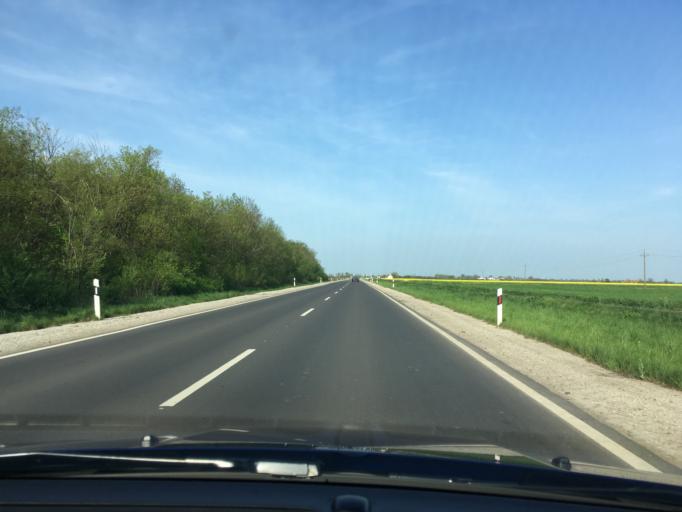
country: HU
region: Bekes
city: Csorvas
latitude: 46.6455
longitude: 20.8966
